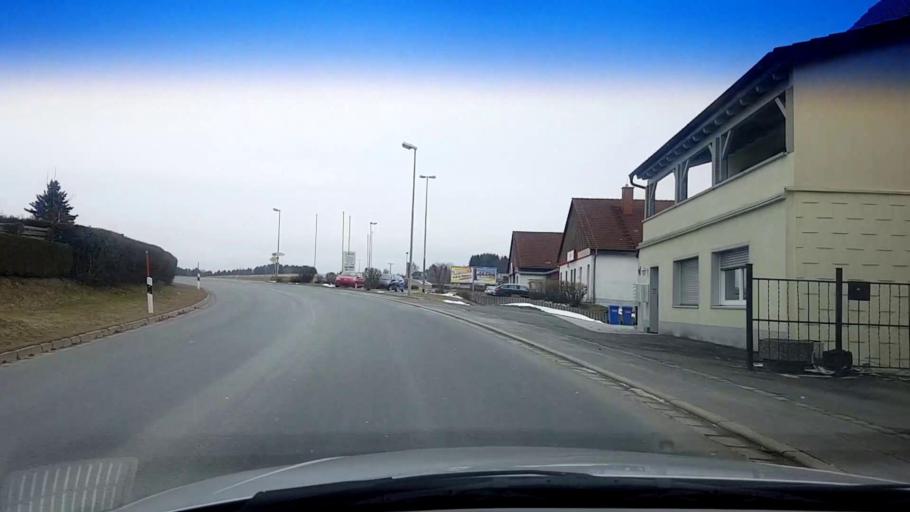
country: DE
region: Bavaria
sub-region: Upper Franconia
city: Marktleugast
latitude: 50.1689
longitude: 11.6371
